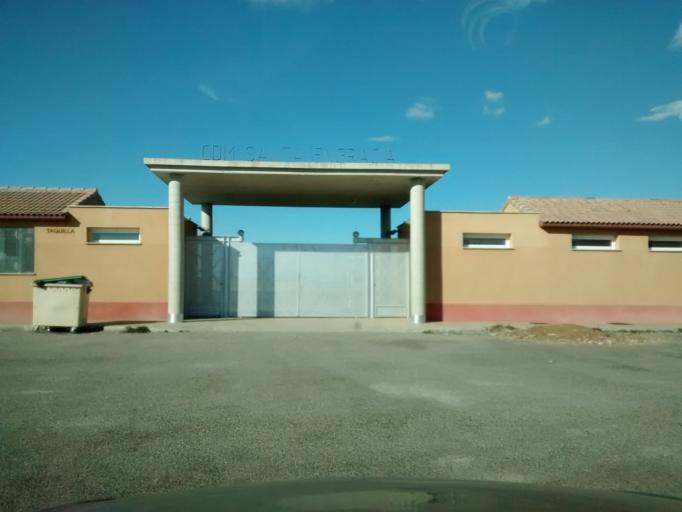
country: ES
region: Aragon
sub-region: Provincia de Zaragoza
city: San Mateo de Gallego
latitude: 41.8339
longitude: -0.7587
